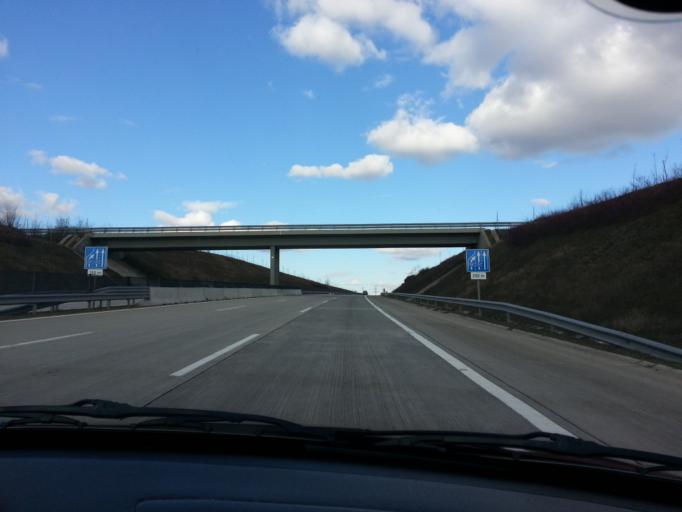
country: HU
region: Pest
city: Nagytarcsa
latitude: 47.5339
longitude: 19.3050
